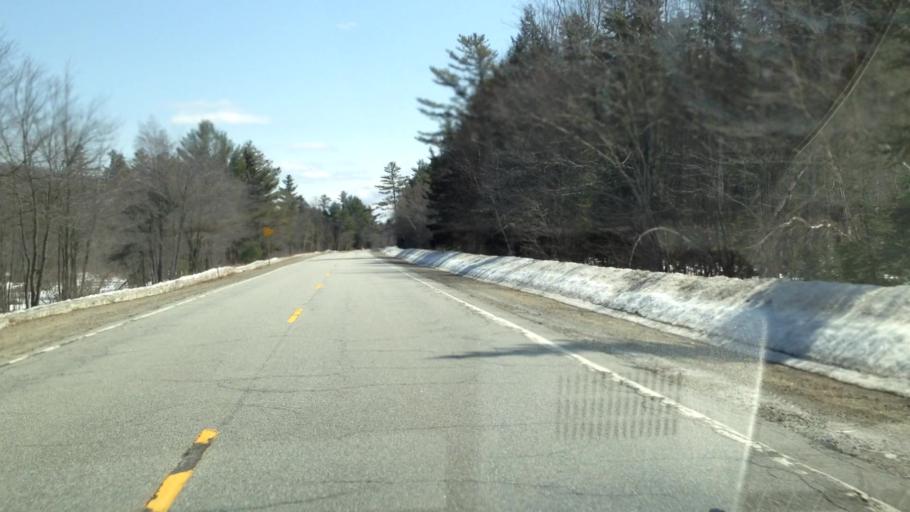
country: US
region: New Hampshire
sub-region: Sullivan County
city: Springfield
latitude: 43.4951
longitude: -71.9982
